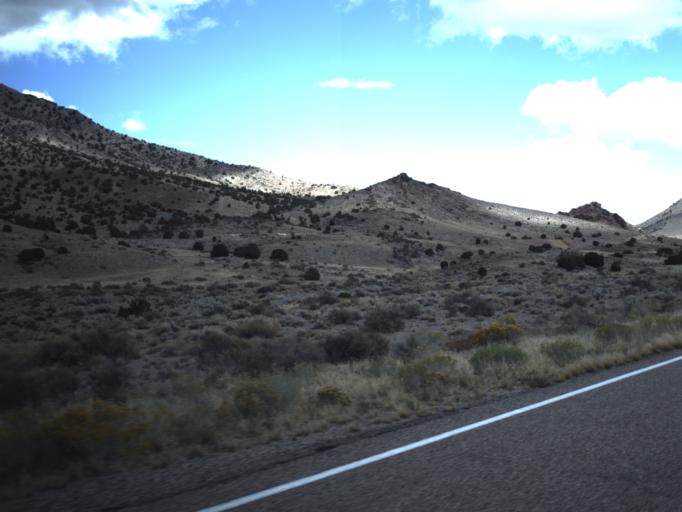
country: US
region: Utah
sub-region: Beaver County
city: Milford
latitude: 38.4345
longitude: -113.2914
